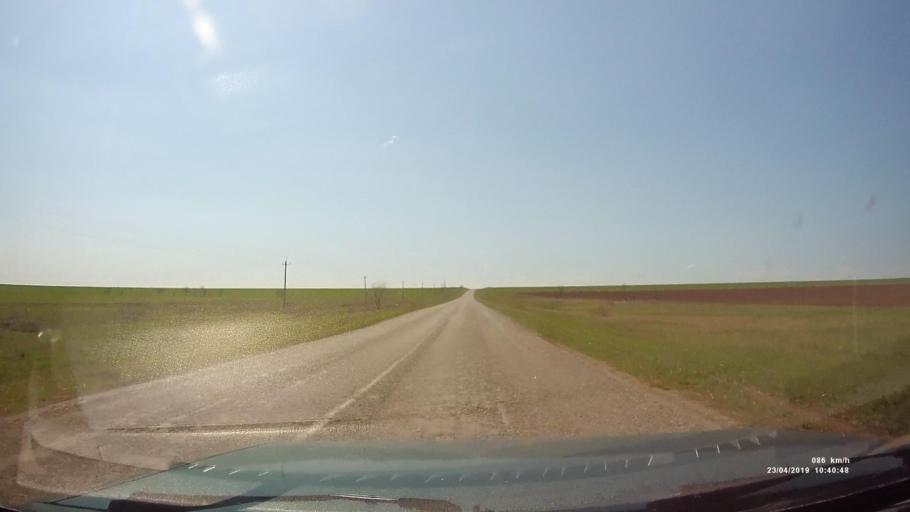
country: RU
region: Kalmykiya
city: Yashalta
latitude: 46.5018
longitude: 42.6384
